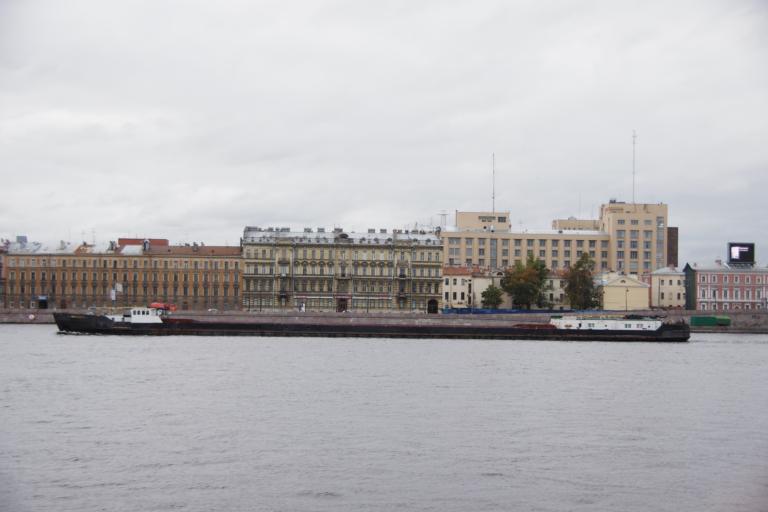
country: RU
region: Leningrad
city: Finlyandskiy
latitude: 59.9533
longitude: 30.3520
